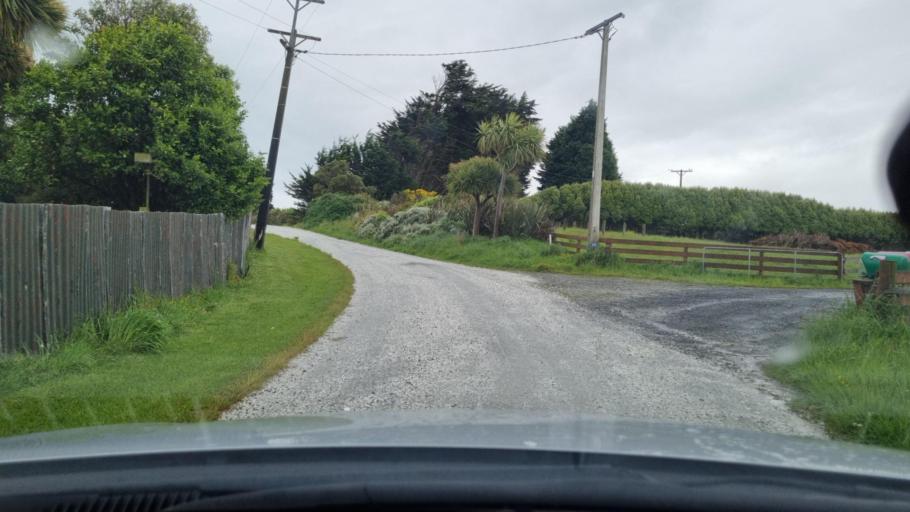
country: NZ
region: Southland
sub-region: Invercargill City
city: Bluff
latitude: -46.5389
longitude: 168.2904
